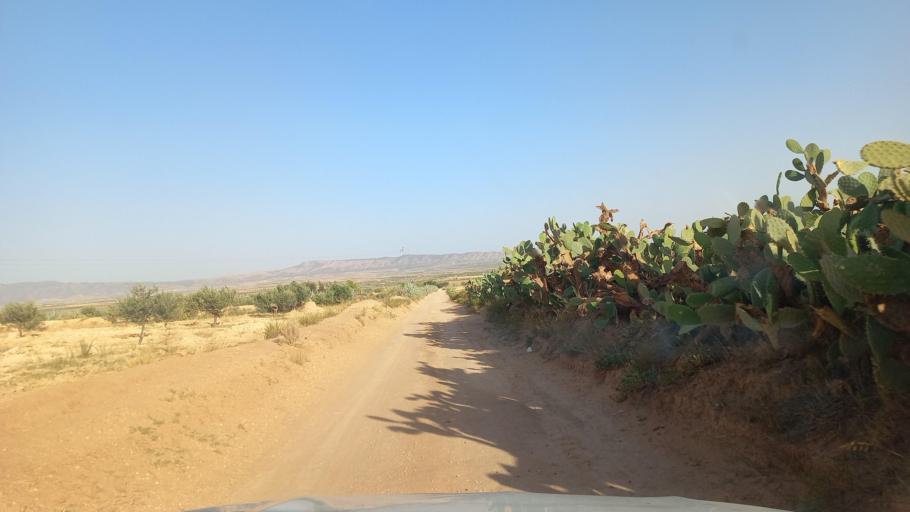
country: TN
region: Al Qasrayn
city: Sbiba
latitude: 35.3664
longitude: 9.0137
